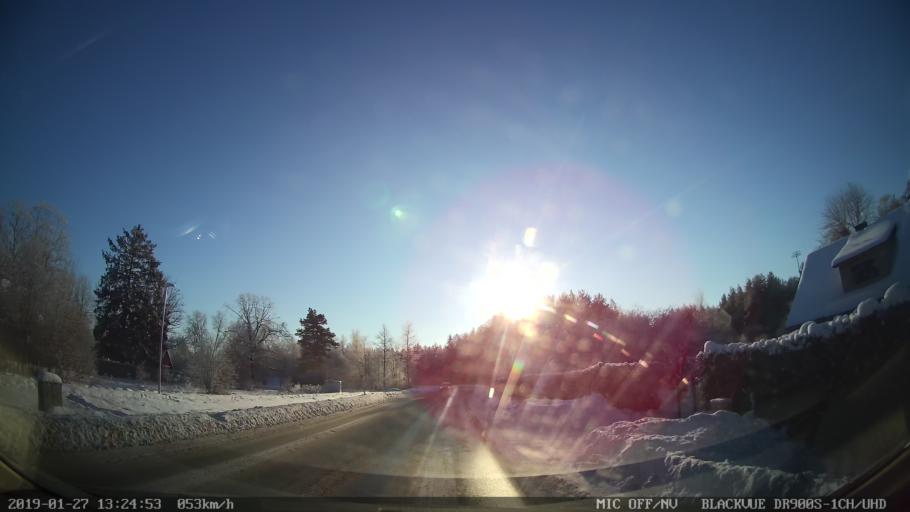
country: EE
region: Harju
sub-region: Tallinna linn
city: Tallinn
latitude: 59.3965
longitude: 24.7927
